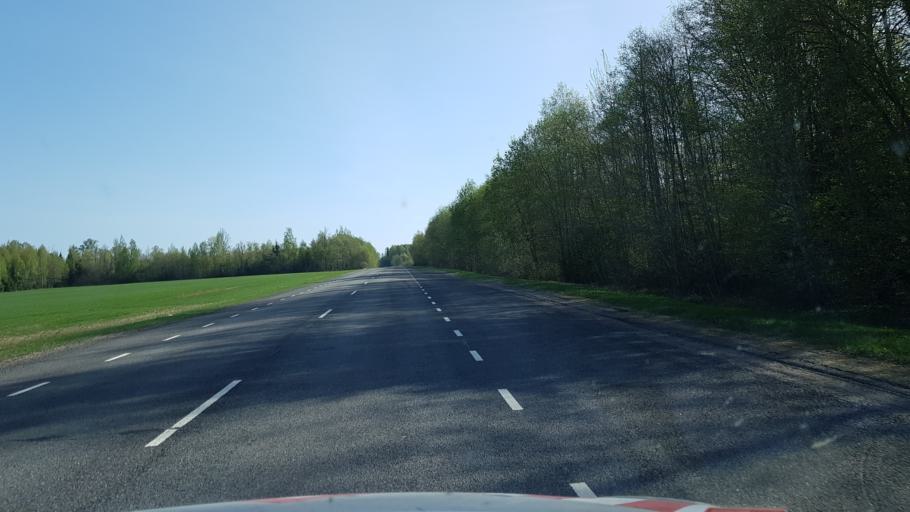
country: EE
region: Viljandimaa
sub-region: Karksi vald
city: Karksi-Nuia
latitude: 58.2139
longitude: 25.5520
